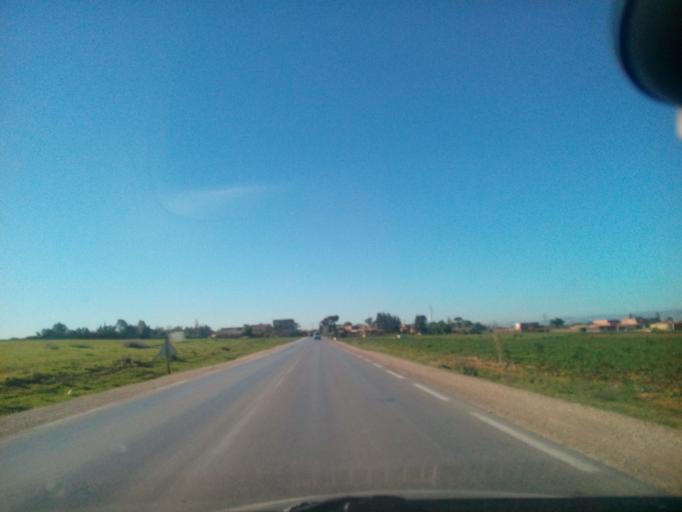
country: DZ
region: Relizane
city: Djidiouia
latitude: 35.8925
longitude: 0.7274
